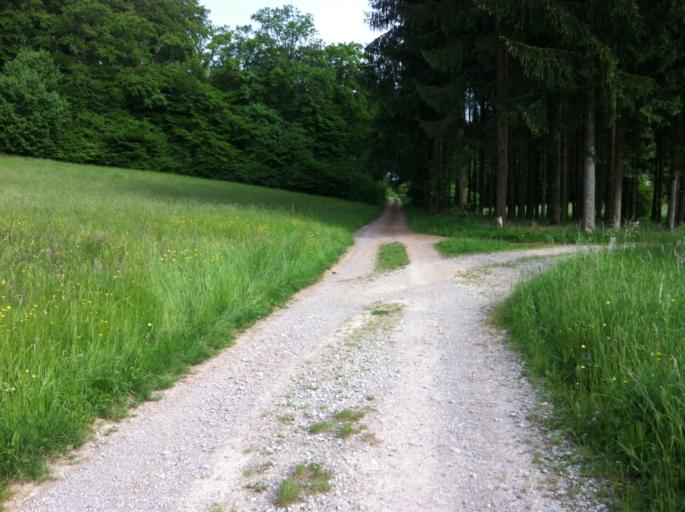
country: DE
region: Baden-Wuerttemberg
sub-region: Freiburg Region
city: Maulburg
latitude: 47.6161
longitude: 7.7870
